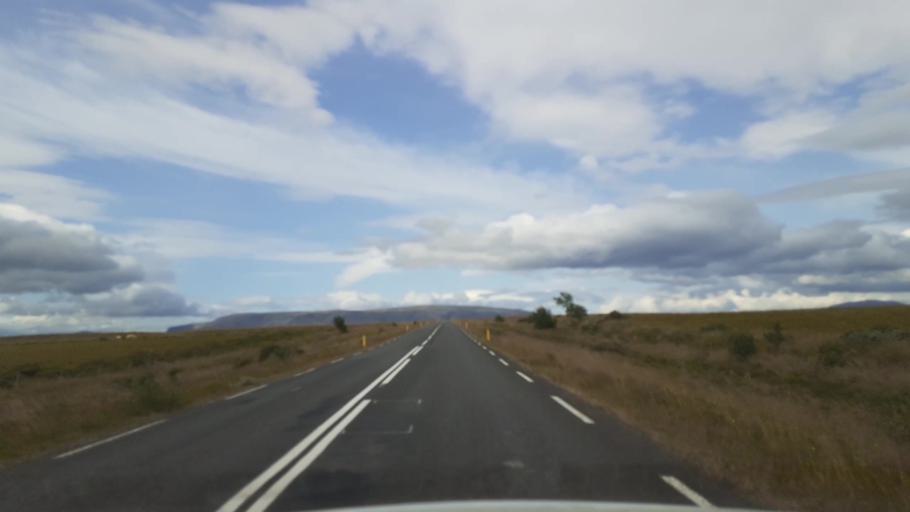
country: IS
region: South
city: Selfoss
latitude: 63.9152
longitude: -20.8380
